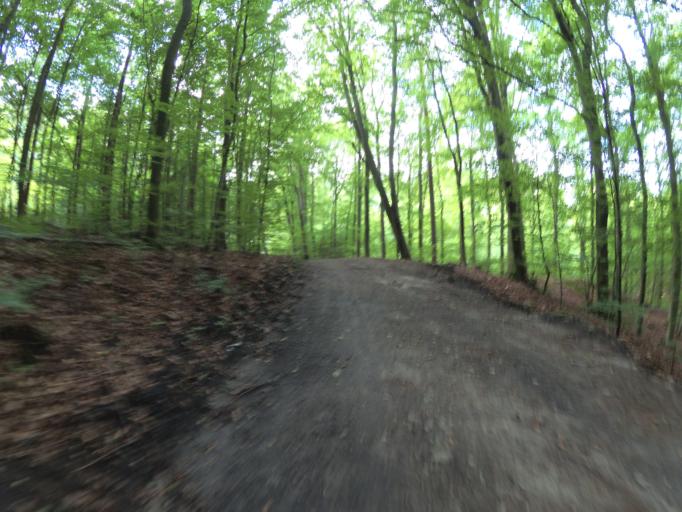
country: PL
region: Pomeranian Voivodeship
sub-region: Gdynia
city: Wielki Kack
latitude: 54.5068
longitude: 18.4488
